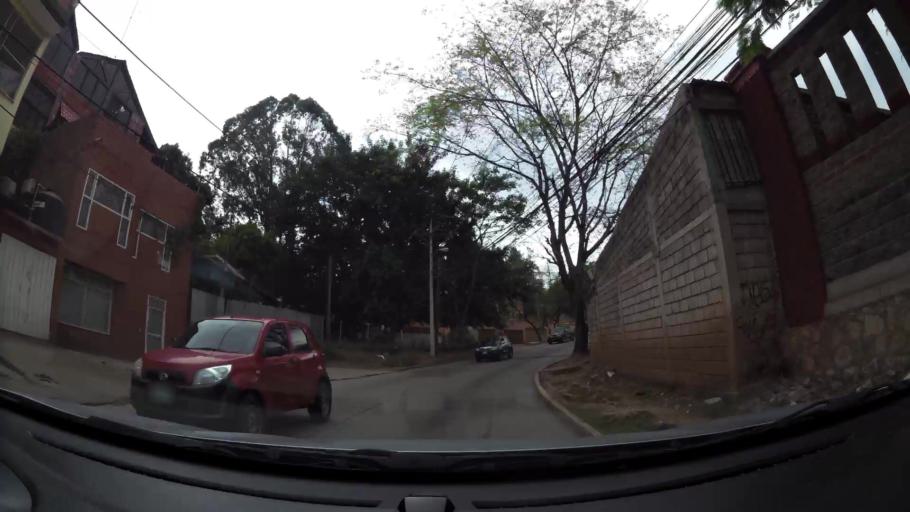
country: HN
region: Francisco Morazan
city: Tegucigalpa
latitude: 14.0917
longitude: -87.1695
